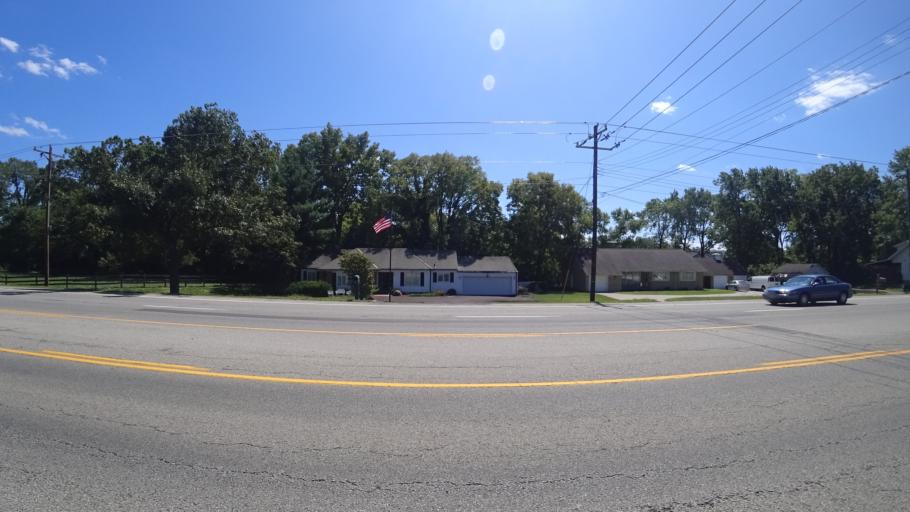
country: US
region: Ohio
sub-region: Butler County
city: New Miami
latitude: 39.4049
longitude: -84.5254
